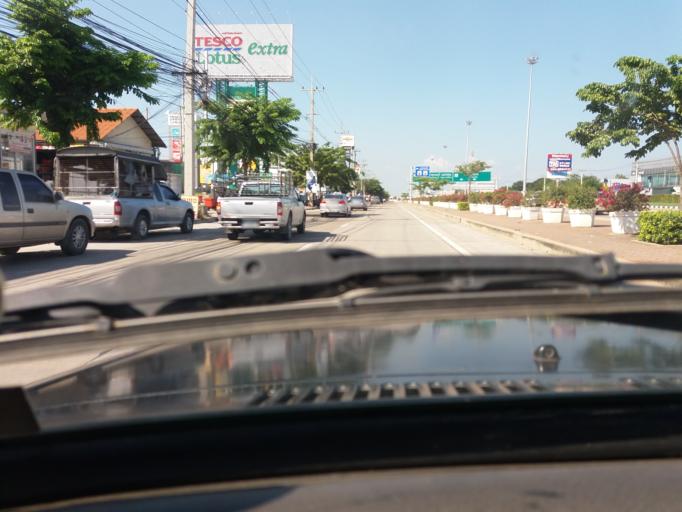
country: TH
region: Suphan Buri
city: Suphan Buri
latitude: 14.4690
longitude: 100.1312
